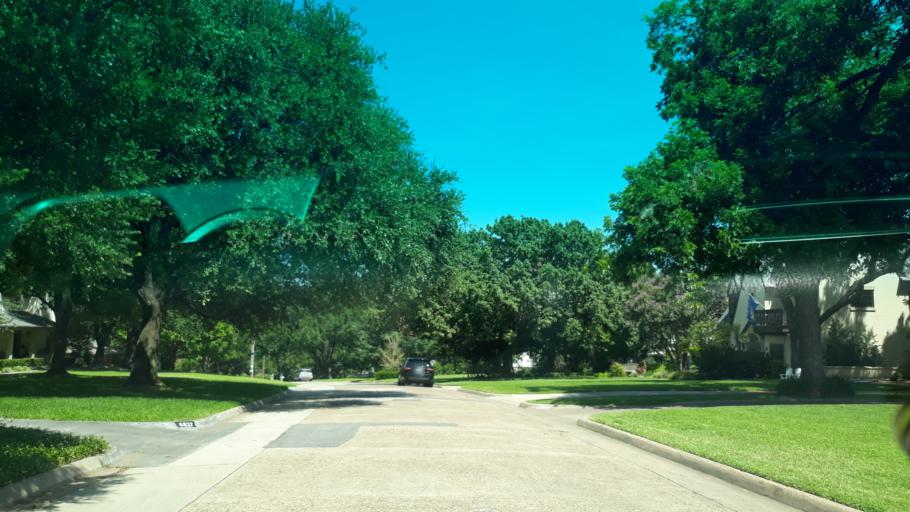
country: US
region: Texas
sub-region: Dallas County
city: Highland Park
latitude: 32.8179
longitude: -96.7429
